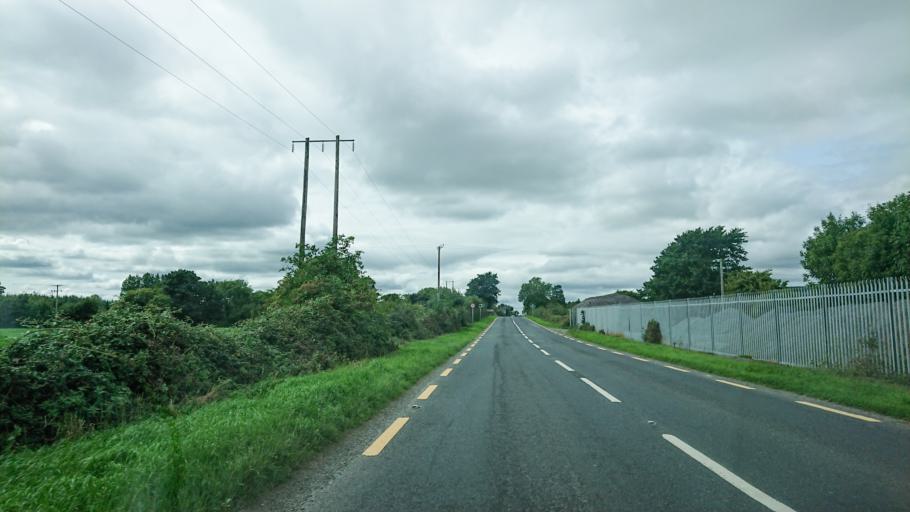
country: IE
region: Munster
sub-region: Waterford
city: Dungarvan
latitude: 52.1077
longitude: -7.6585
